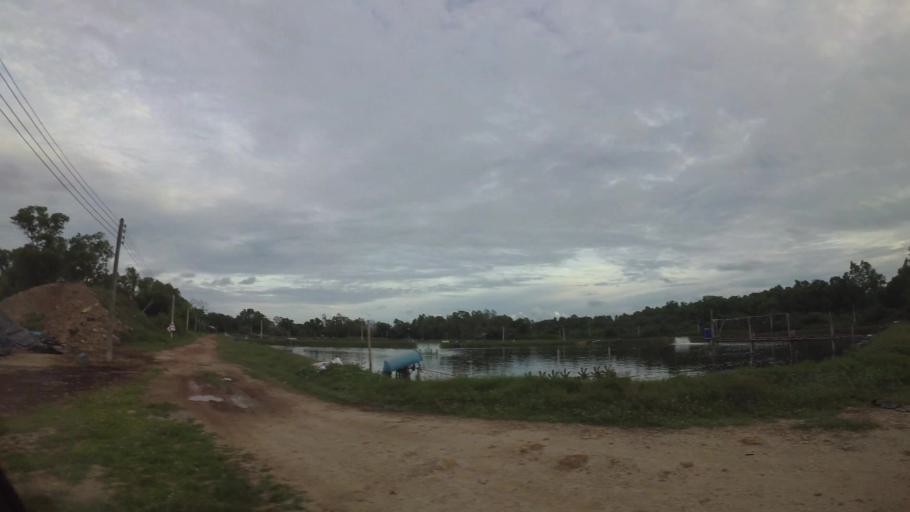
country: TH
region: Rayong
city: Rayong
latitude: 12.6739
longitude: 101.2549
